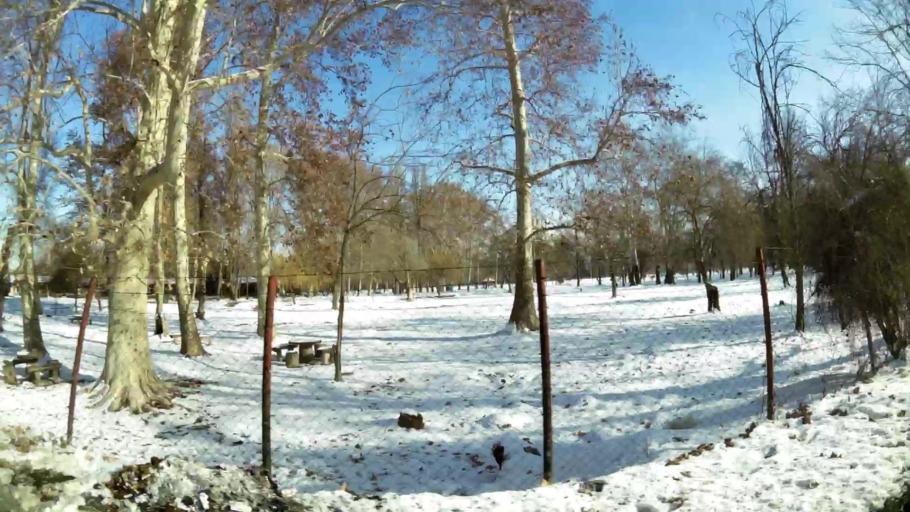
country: MK
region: Saraj
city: Saraj
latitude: 42.0008
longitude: 21.3372
